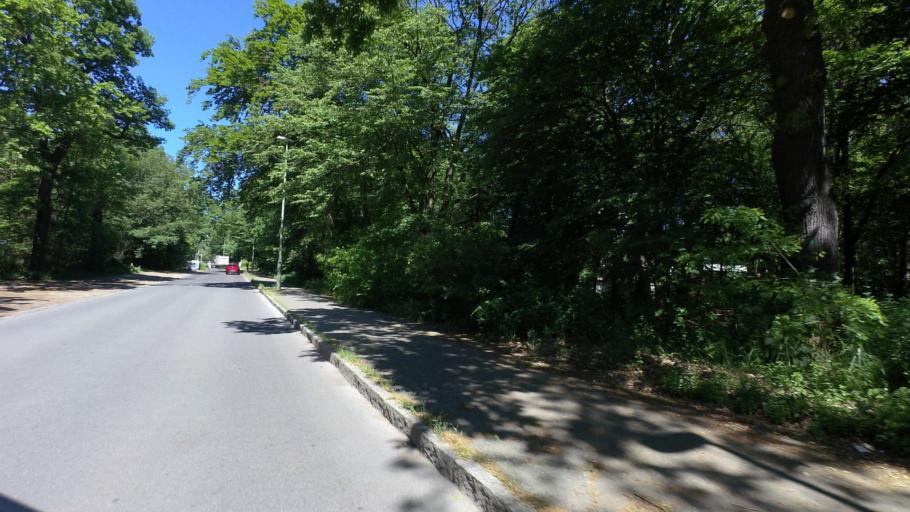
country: DE
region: Berlin
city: Siemensstadt
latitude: 52.5470
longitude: 13.2713
